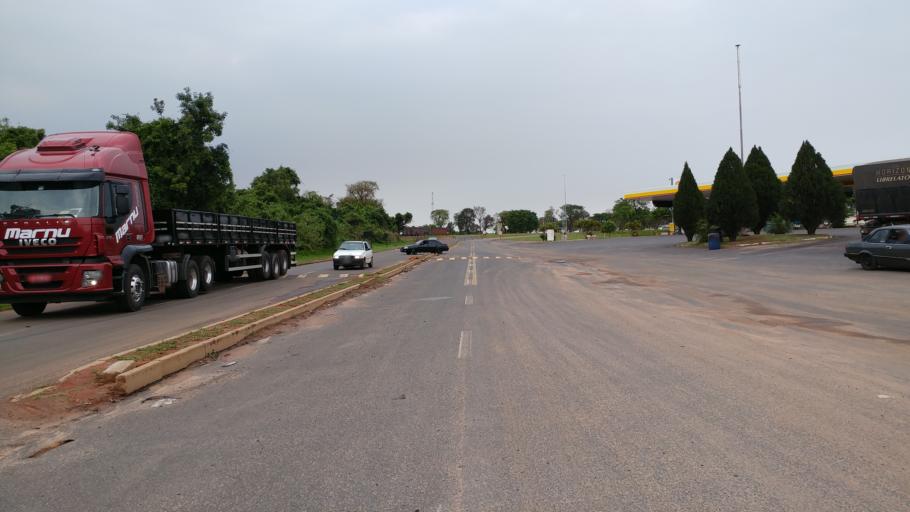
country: BR
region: Sao Paulo
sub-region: Paraguacu Paulista
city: Paraguacu Paulista
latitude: -22.4436
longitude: -50.5825
